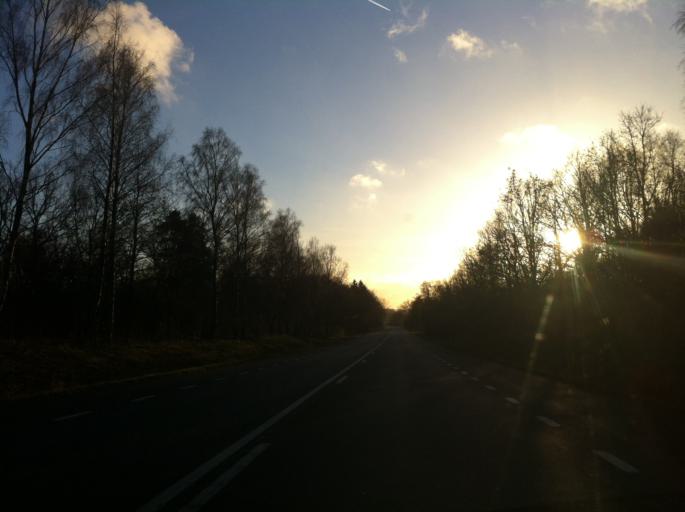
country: SE
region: Skane
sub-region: Hassleholms Kommun
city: Hassleholm
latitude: 56.1337
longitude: 13.7999
